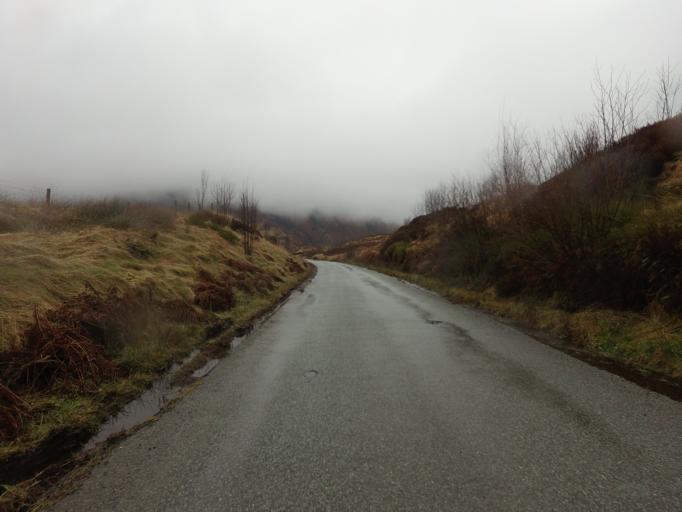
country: GB
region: Scotland
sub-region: West Dunbartonshire
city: Balloch
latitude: 56.2481
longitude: -4.5860
